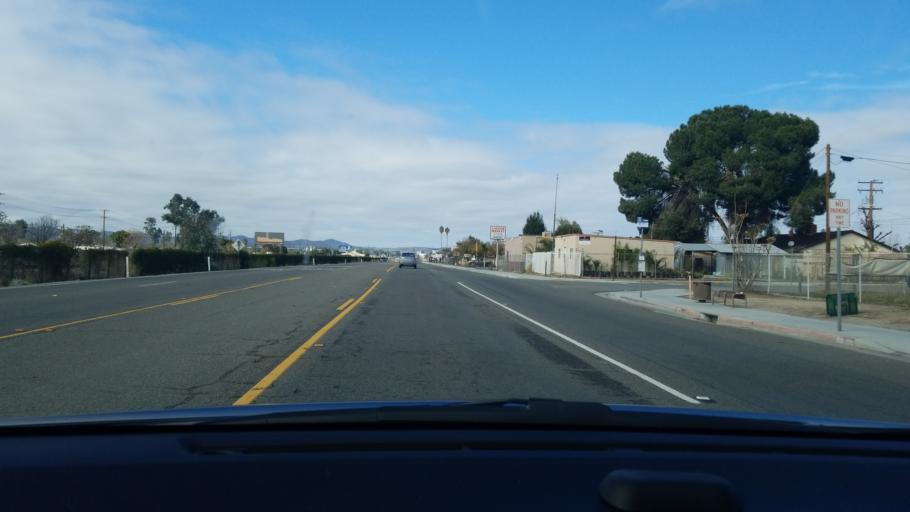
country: US
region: California
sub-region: Riverside County
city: Romoland
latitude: 33.7447
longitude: -117.1734
